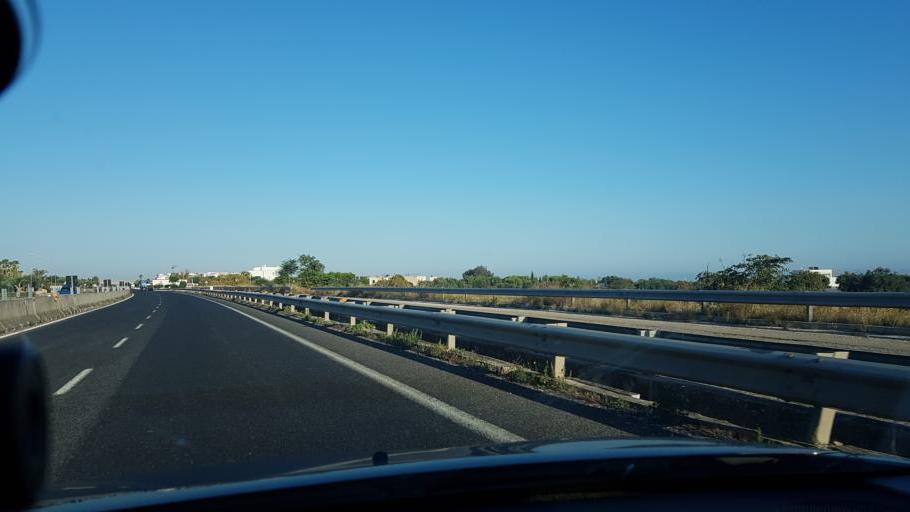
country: IT
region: Apulia
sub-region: Provincia di Bari
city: Monopoli
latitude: 40.9254
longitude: 17.3118
